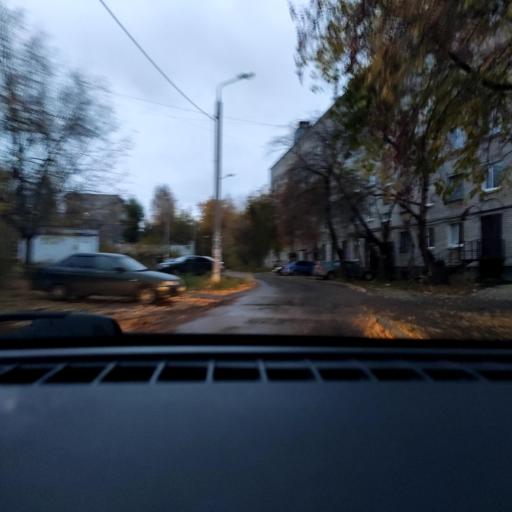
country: RU
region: Perm
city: Perm
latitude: 57.9613
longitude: 56.2255
